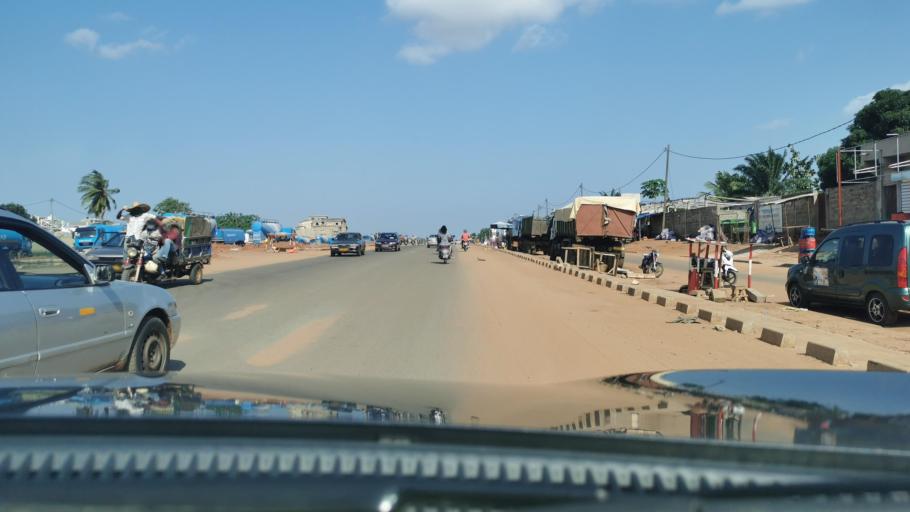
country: TG
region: Maritime
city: Lome
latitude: 6.2120
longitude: 1.1350
